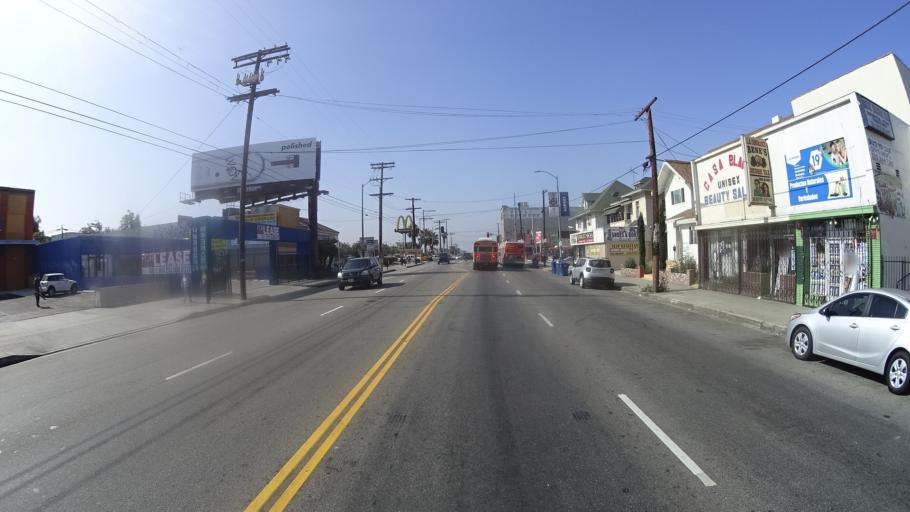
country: US
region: California
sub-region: Los Angeles County
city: Echo Park
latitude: 34.0452
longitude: -118.2916
